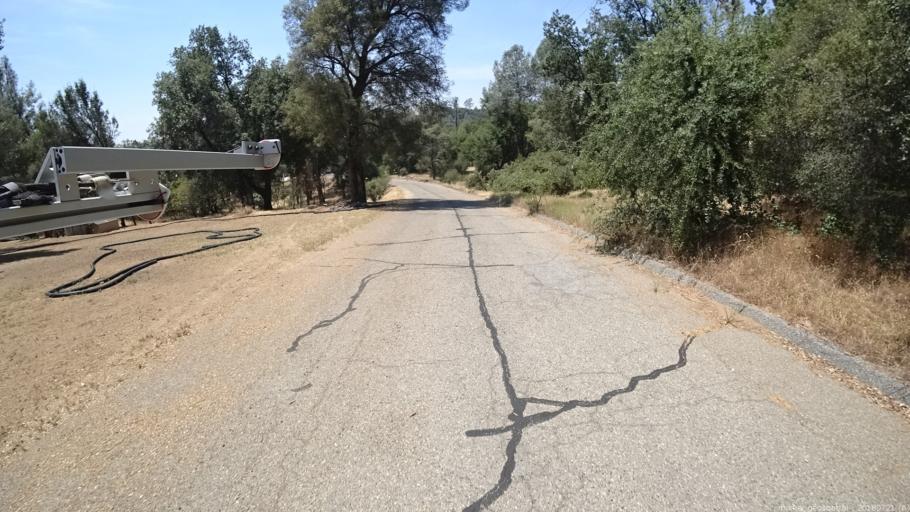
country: US
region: California
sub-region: Madera County
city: Oakhurst
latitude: 37.2527
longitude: -119.5438
